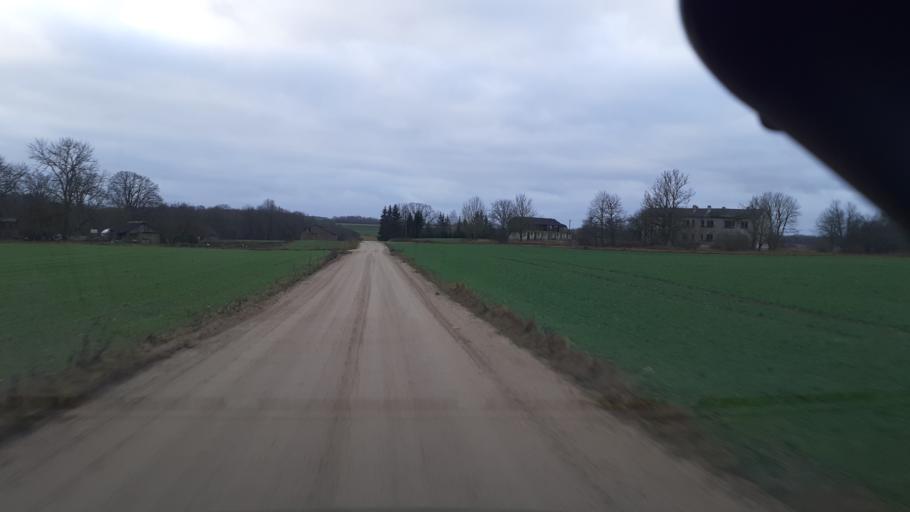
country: LV
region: Aizpute
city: Aizpute
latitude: 56.8511
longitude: 21.7627
